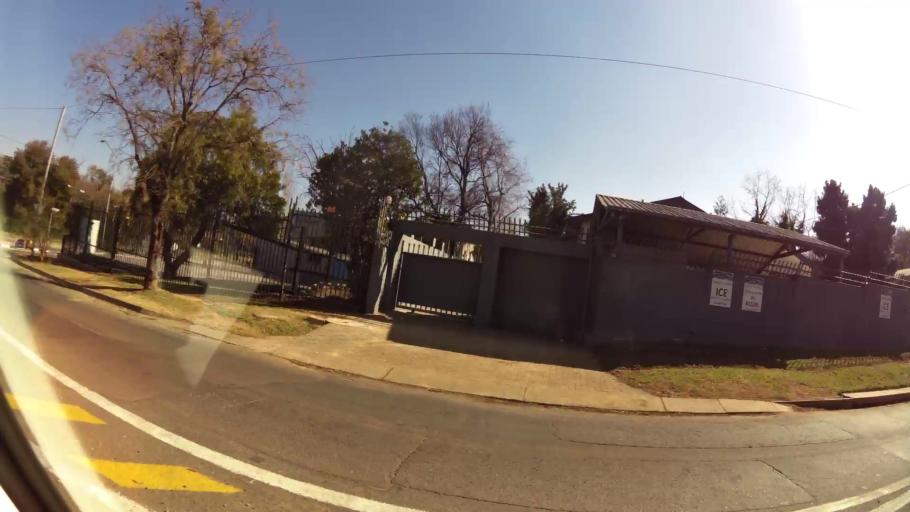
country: ZA
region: Gauteng
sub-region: City of Tshwane Metropolitan Municipality
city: Pretoria
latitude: -25.7774
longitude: 28.2661
